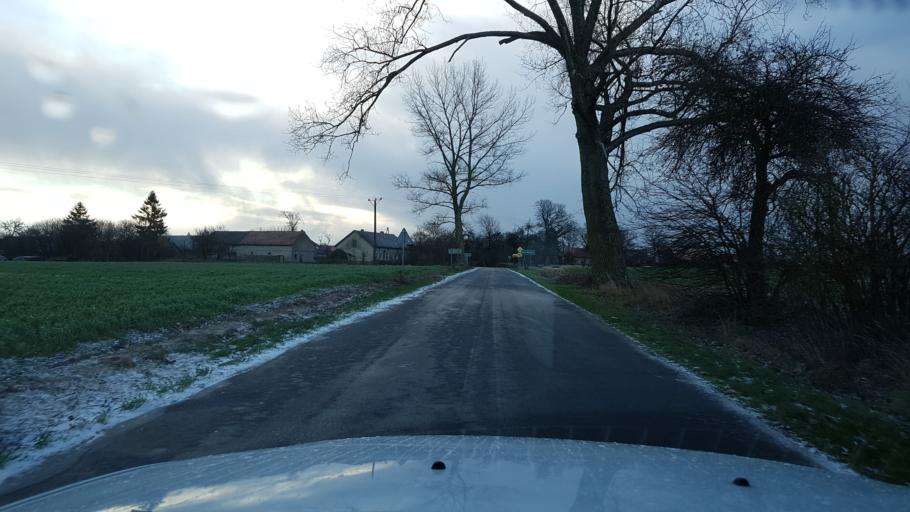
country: PL
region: West Pomeranian Voivodeship
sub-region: Powiat gryficki
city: Brojce
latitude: 54.0362
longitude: 15.3588
